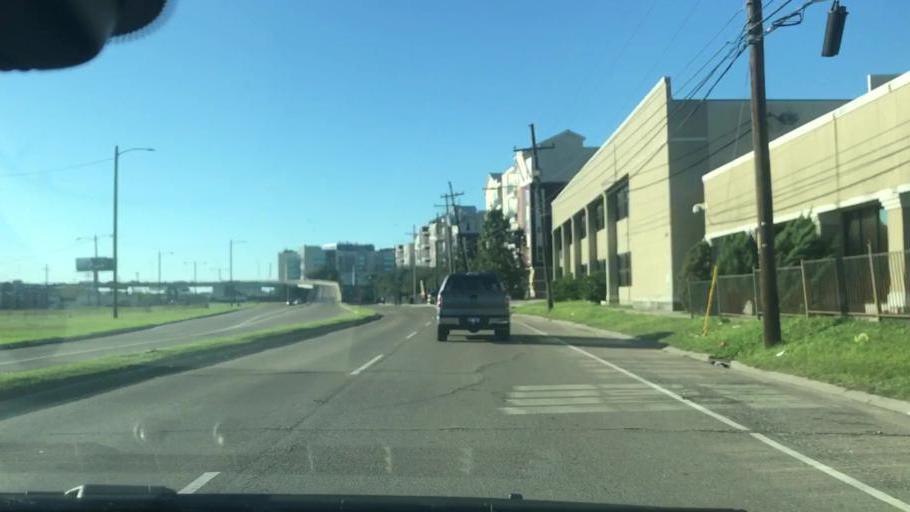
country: US
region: Louisiana
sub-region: Orleans Parish
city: New Orleans
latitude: 29.9574
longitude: -90.0897
